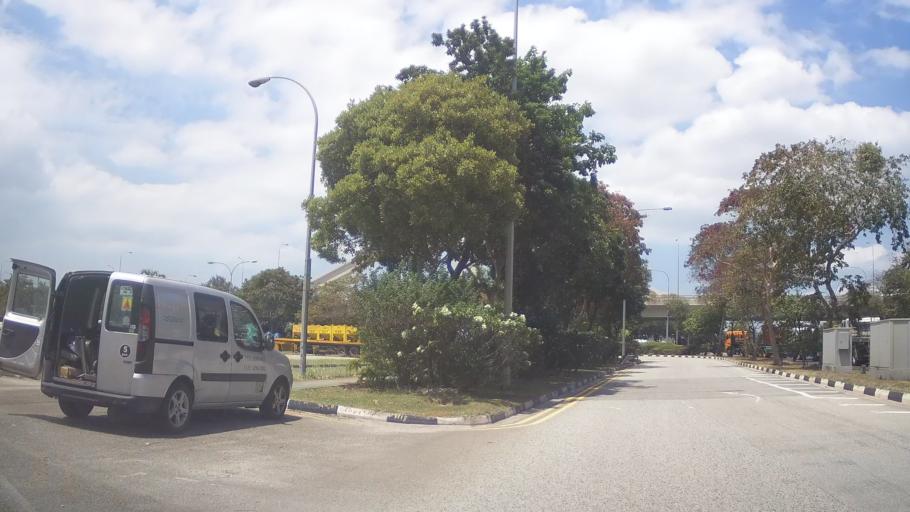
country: SG
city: Singapore
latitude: 1.3140
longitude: 103.7113
